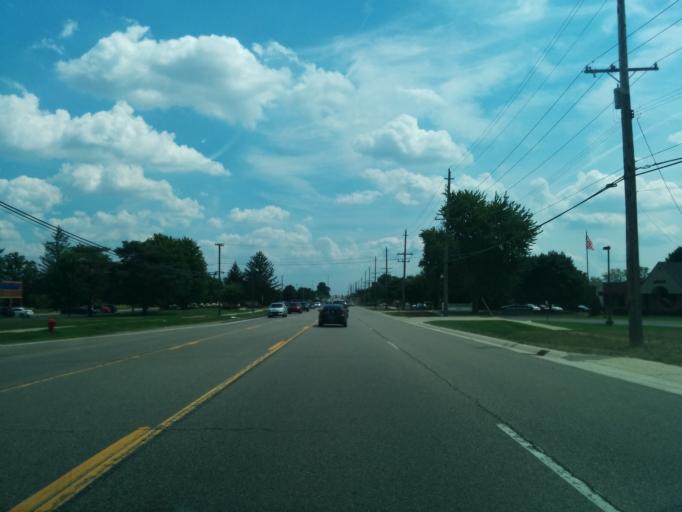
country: US
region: Michigan
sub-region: Oakland County
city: Novi
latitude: 42.4731
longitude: -83.4410
